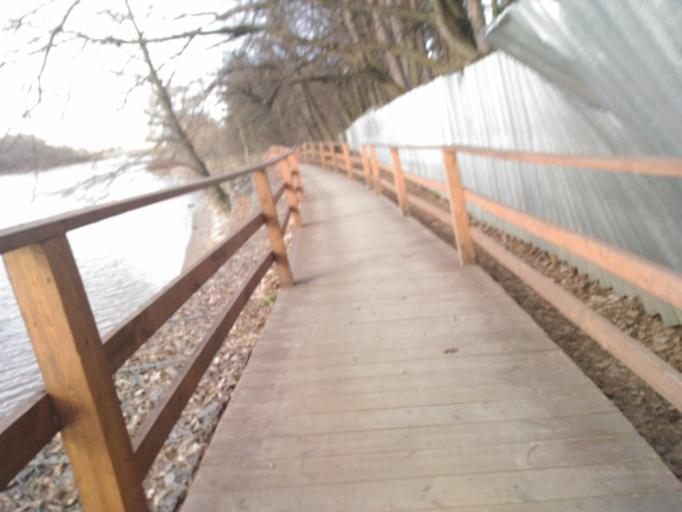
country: RU
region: Moscow
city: Strogino
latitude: 55.7842
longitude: 37.4072
